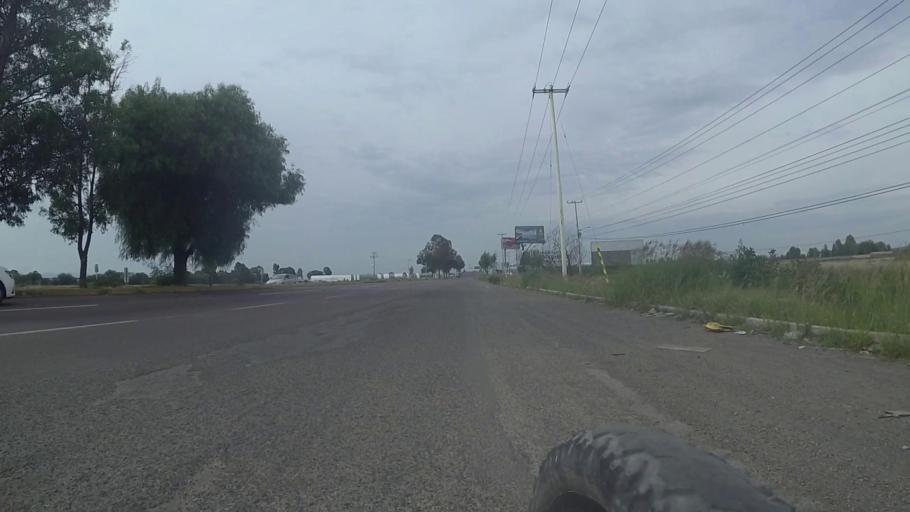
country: MX
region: Aguascalientes
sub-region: Aguascalientes
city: Penuelas (El Cienegal)
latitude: 21.7431
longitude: -102.2768
